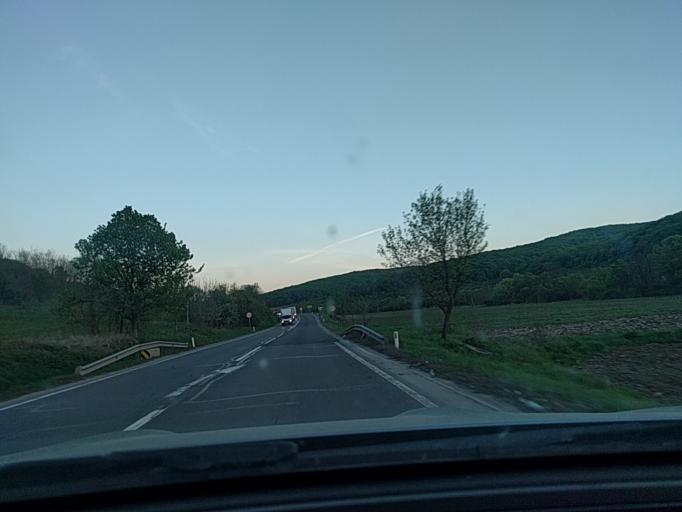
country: RO
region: Mures
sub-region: Comuna Nades
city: Nades
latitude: 46.3298
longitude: 24.7116
